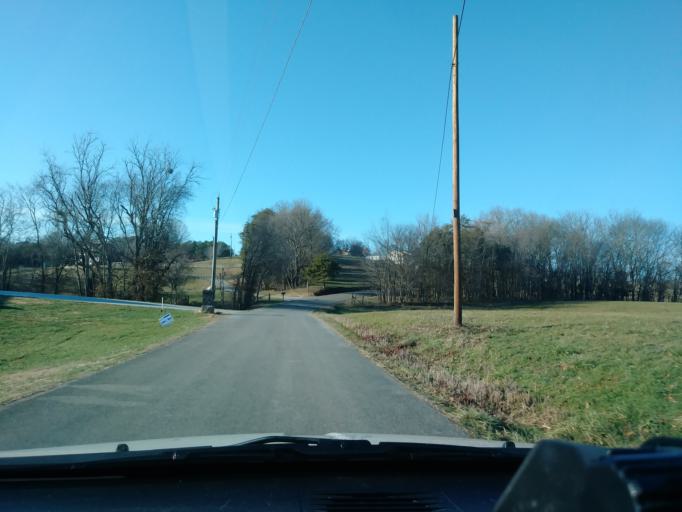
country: US
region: Tennessee
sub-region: Greene County
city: Greeneville
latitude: 36.0742
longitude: -82.9025
